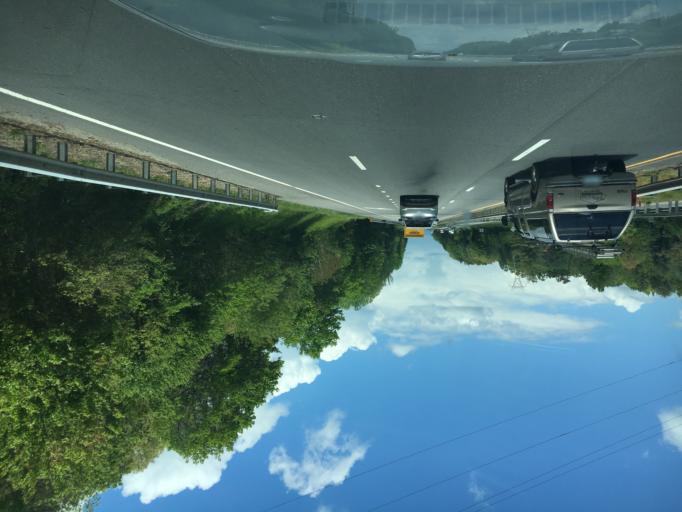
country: US
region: North Carolina
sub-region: Buncombe County
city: Weaverville
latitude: 35.6736
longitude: -82.5840
